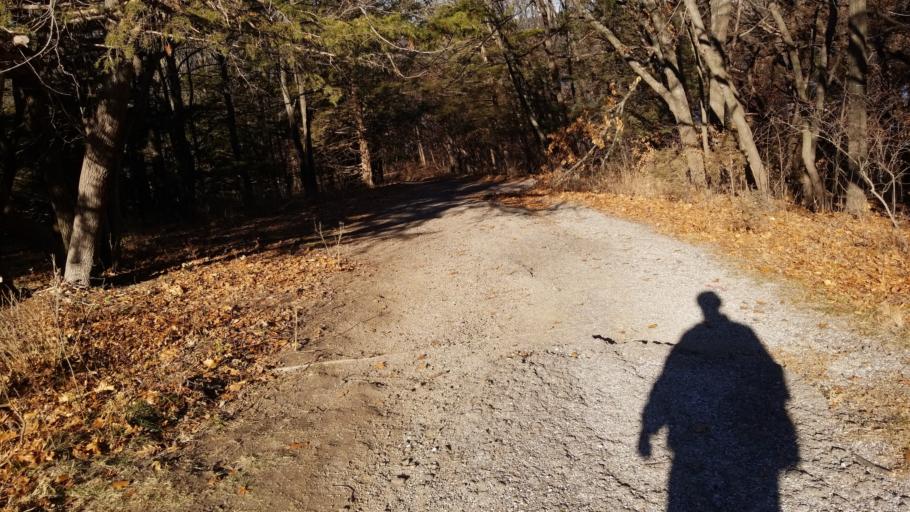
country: US
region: Nebraska
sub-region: Cass County
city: Louisville
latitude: 40.9912
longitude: -96.2143
